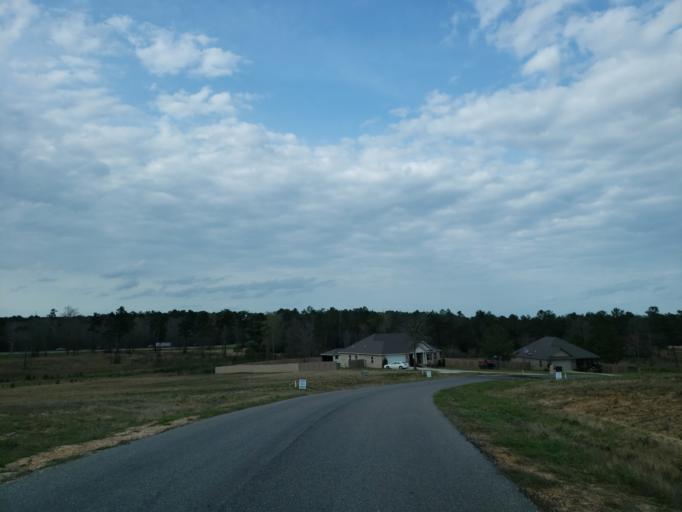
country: US
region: Mississippi
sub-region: Jones County
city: Ellisville
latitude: 31.5630
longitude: -89.2519
